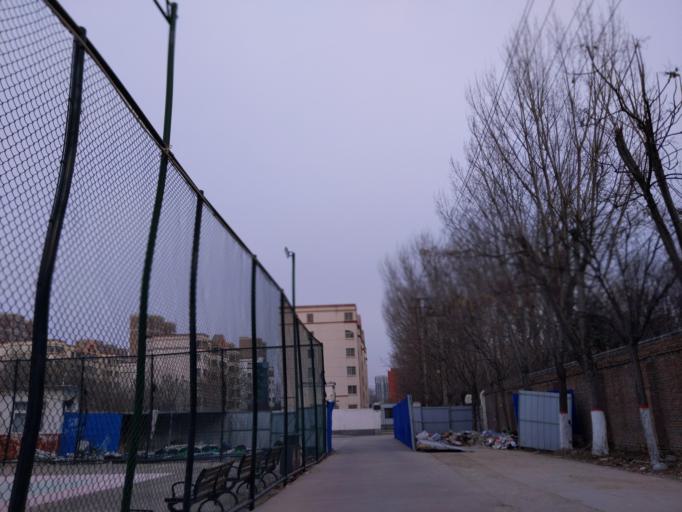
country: CN
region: Henan Sheng
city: Zhongyuanlu
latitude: 35.7552
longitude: 115.0527
